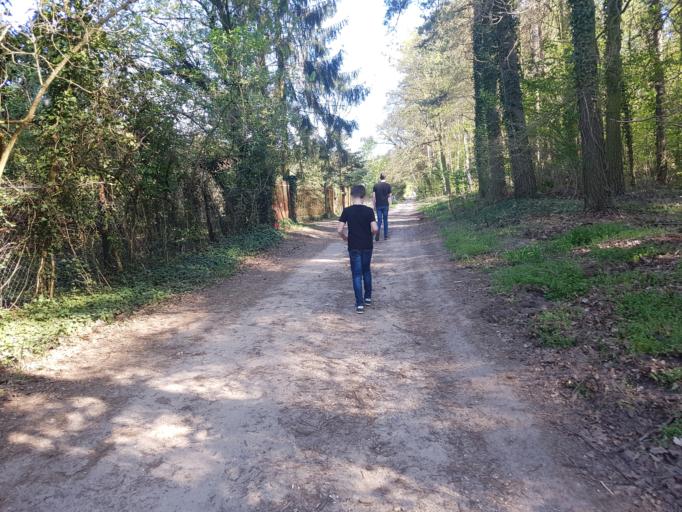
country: DE
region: Brandenburg
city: Groden
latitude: 51.3980
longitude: 13.5666
